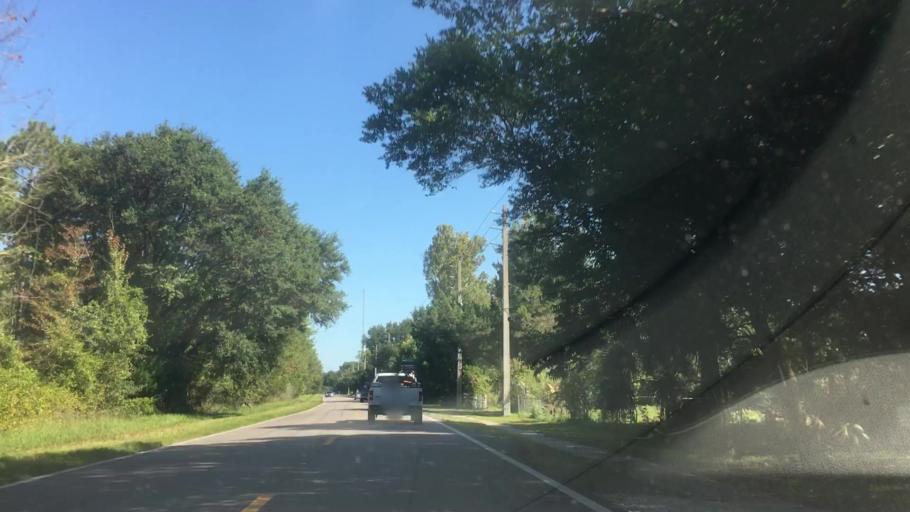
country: US
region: Florida
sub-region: Nassau County
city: Yulee
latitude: 30.4914
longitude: -81.5883
